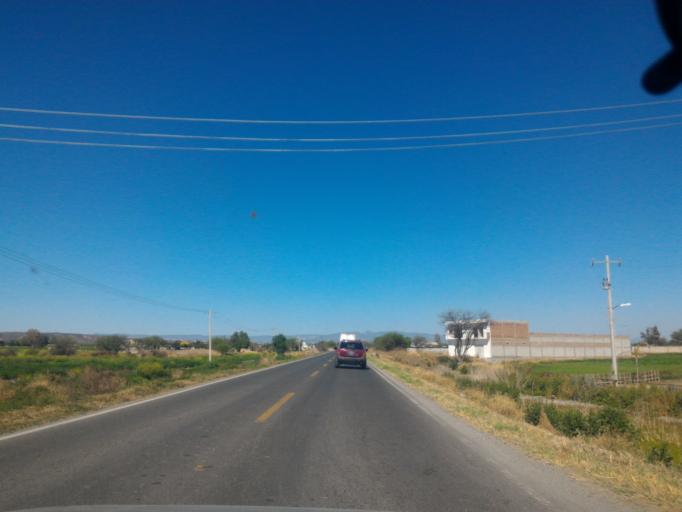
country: MX
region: Guanajuato
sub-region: San Francisco del Rincon
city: San Roque de Montes
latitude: 21.0151
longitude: -101.7967
